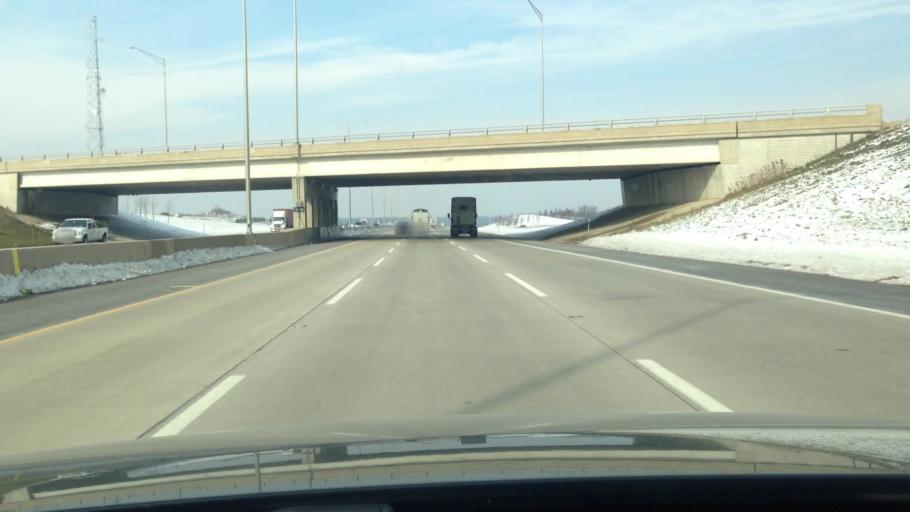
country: US
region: Illinois
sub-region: Cook County
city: Lemont
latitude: 41.6556
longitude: -88.0175
